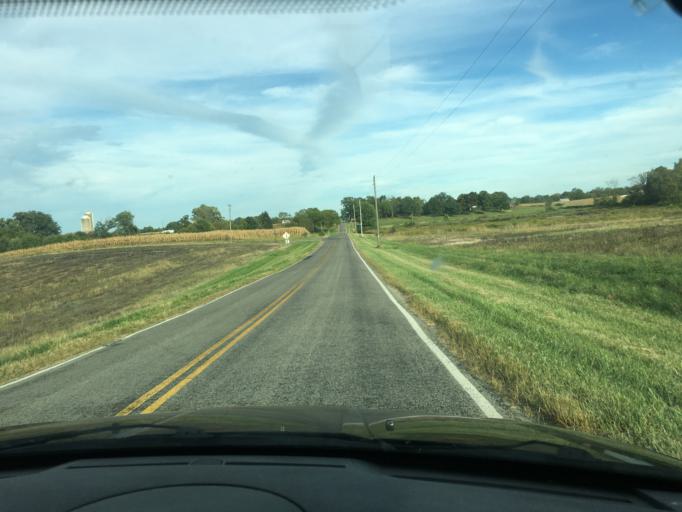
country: US
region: Ohio
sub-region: Logan County
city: West Liberty
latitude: 40.1955
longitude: -83.8093
